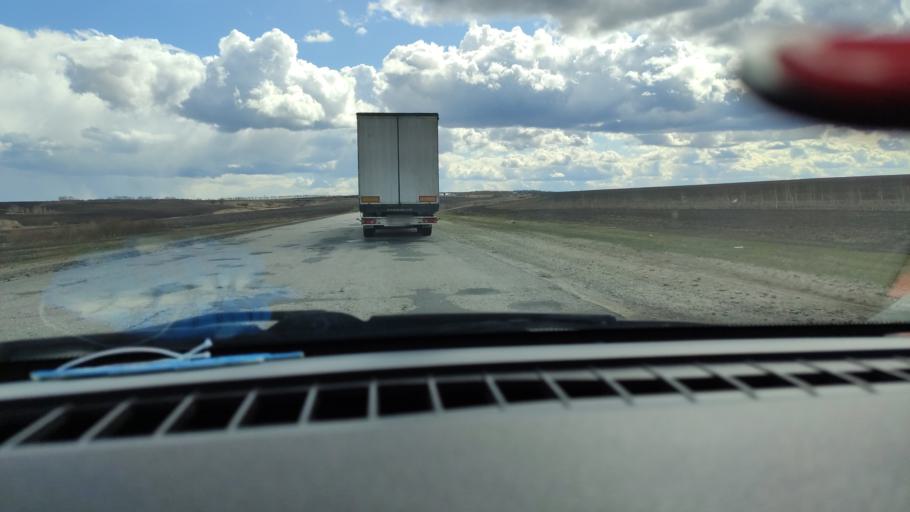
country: RU
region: Samara
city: Varlamovo
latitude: 53.0117
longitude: 48.3323
